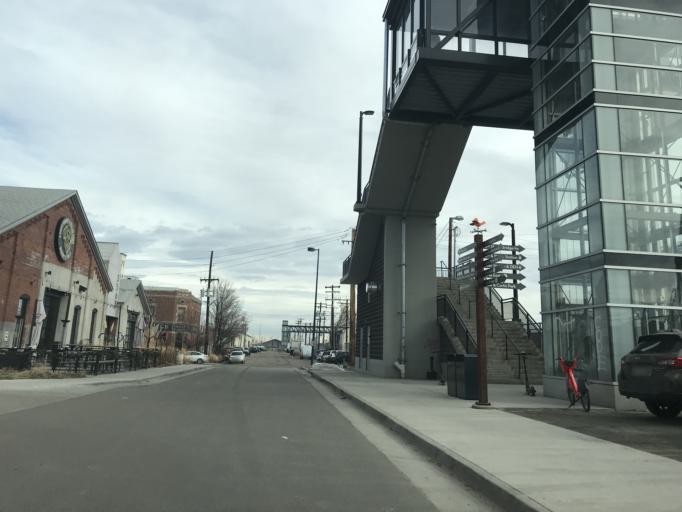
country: US
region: Colorado
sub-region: Denver County
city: Denver
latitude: 39.7695
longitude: -104.9765
